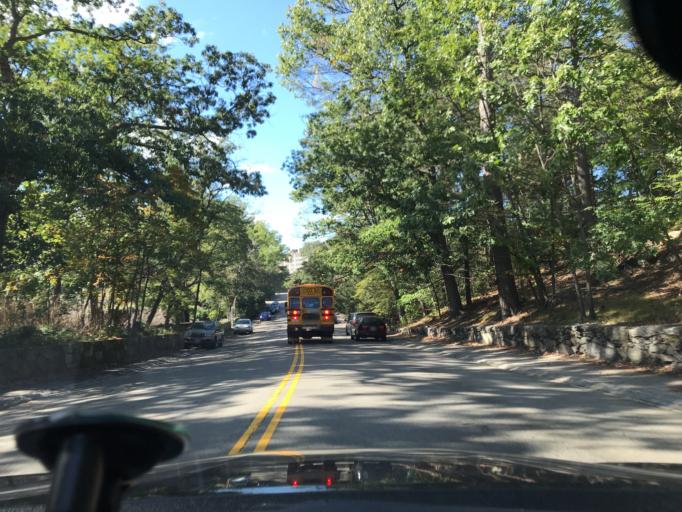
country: US
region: Massachusetts
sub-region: Suffolk County
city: Jamaica Plain
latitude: 42.2961
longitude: -71.1259
